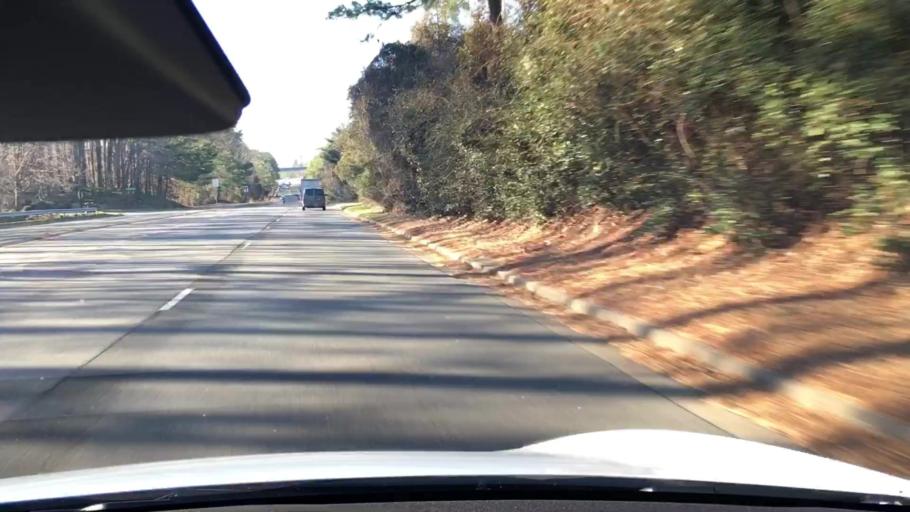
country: US
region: Virginia
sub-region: Henrico County
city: Tuckahoe
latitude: 37.5778
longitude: -77.5714
